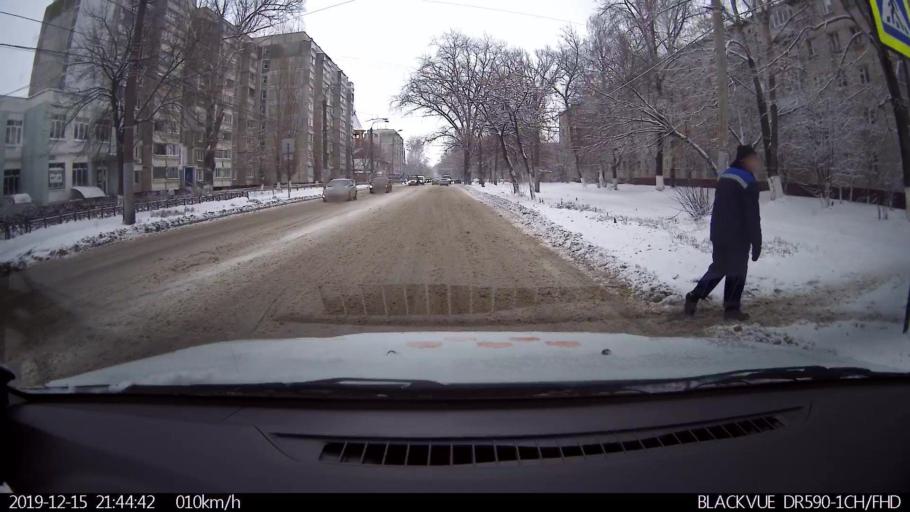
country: RU
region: Nizjnij Novgorod
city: Burevestnik
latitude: 56.2338
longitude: 43.8769
